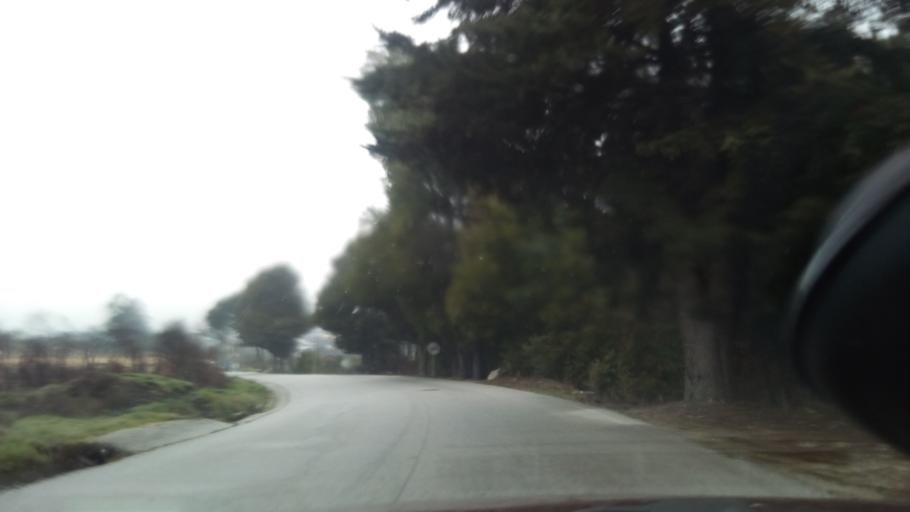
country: PT
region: Viseu
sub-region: Mangualde
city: Mangualde
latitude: 40.6148
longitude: -7.7899
